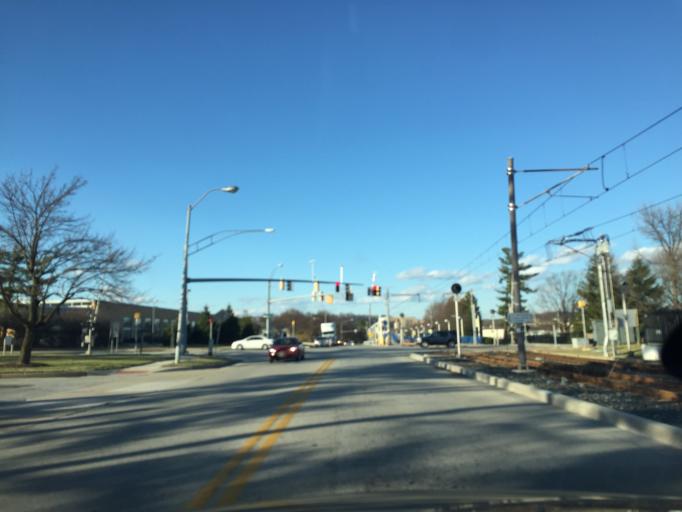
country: US
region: Maryland
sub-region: Baltimore County
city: Cockeysville
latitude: 39.4811
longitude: -76.6621
